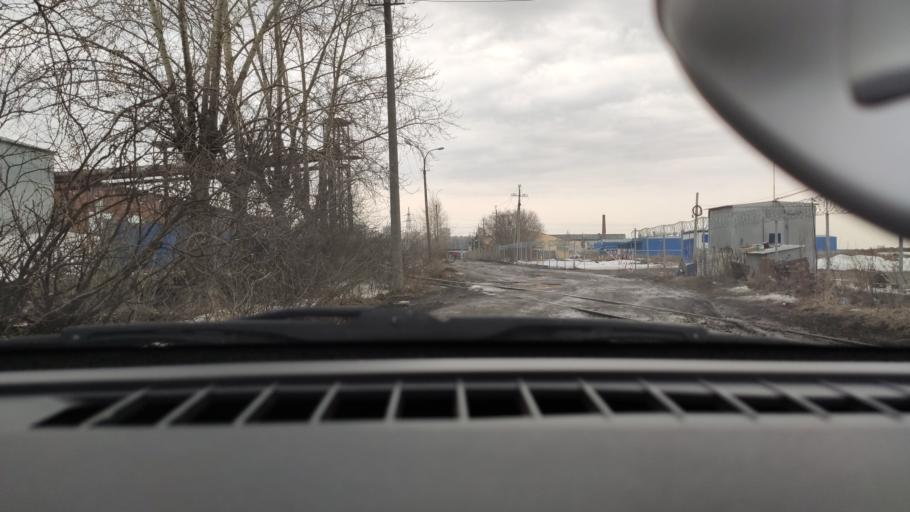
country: RU
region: Perm
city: Perm
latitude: 58.0458
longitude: 56.3146
